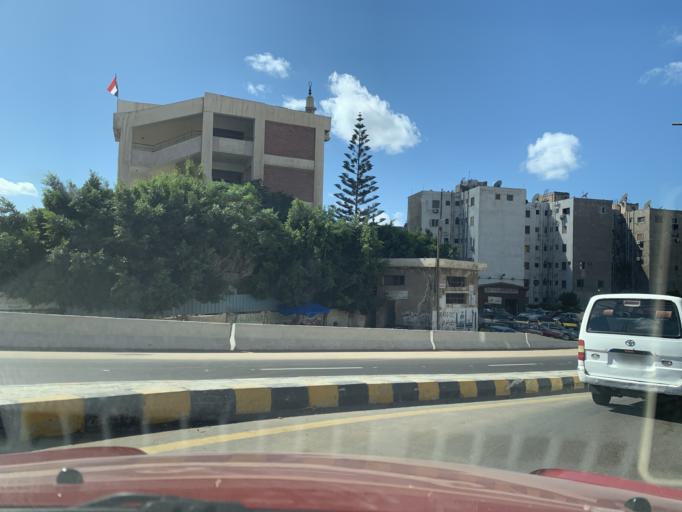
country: EG
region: Alexandria
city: Alexandria
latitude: 31.2142
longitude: 29.9618
